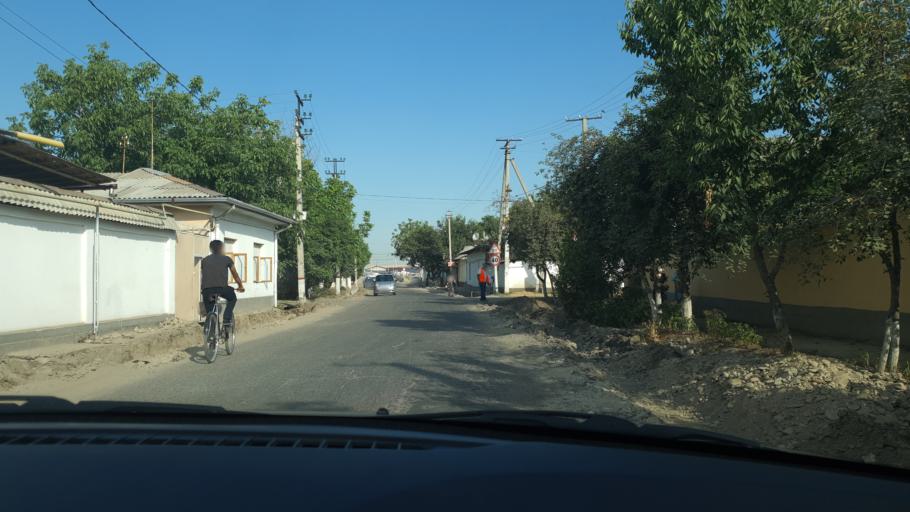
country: UZ
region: Toshkent
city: Urtaowul
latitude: 41.2003
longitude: 69.1579
